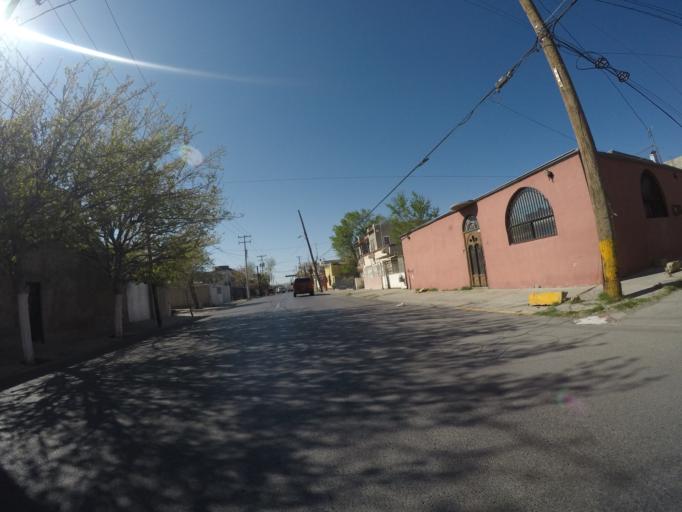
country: MX
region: Chihuahua
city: Ciudad Juarez
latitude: 31.7365
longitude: -106.4741
